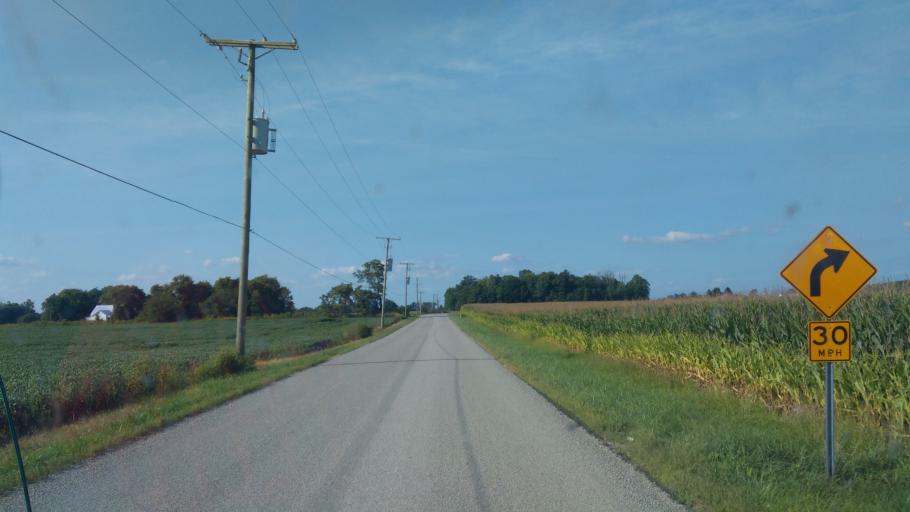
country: US
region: Ohio
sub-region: Hardin County
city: Kenton
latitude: 40.6818
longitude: -83.5761
